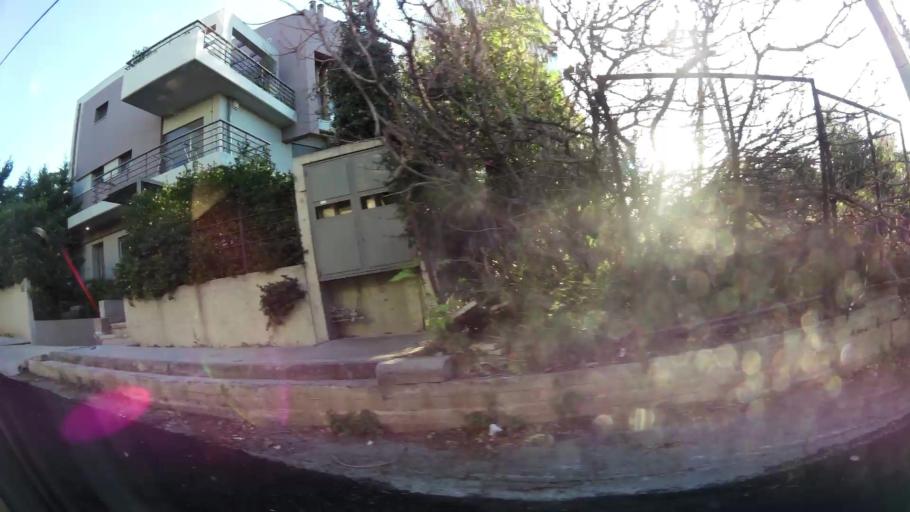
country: GR
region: Attica
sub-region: Nomarchia Athinas
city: Marousi
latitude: 38.0451
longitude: 23.8023
